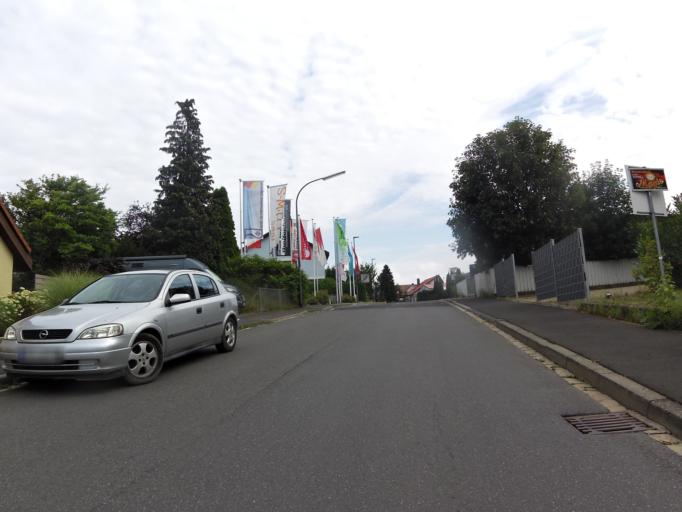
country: DE
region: Bavaria
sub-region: Regierungsbezirk Unterfranken
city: Wuerzburg
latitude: 49.7738
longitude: 9.8711
